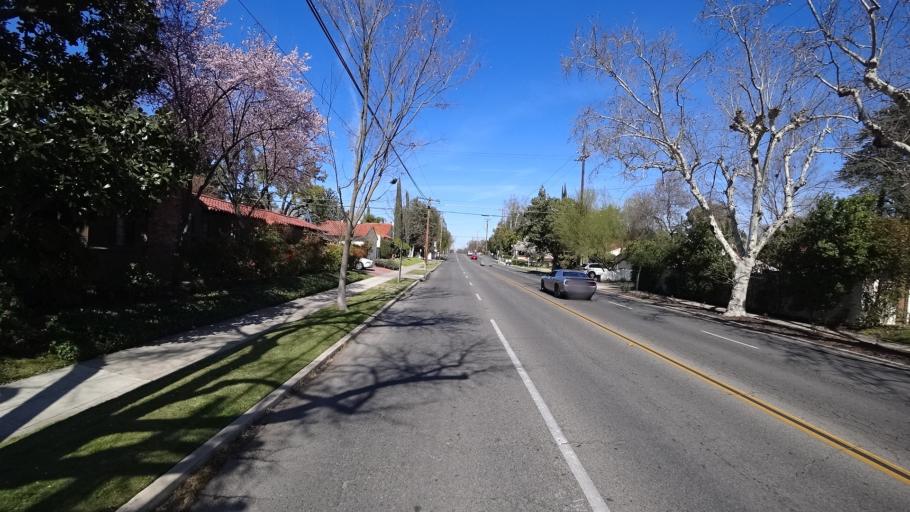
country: US
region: California
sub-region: Fresno County
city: Fresno
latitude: 36.7732
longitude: -119.8087
